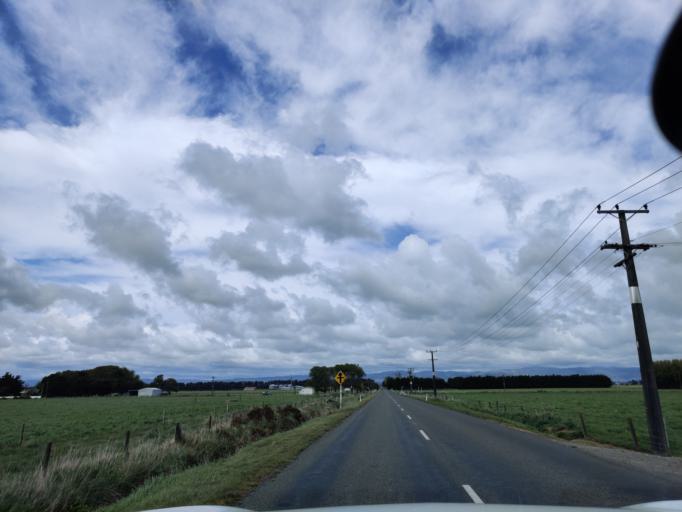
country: NZ
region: Manawatu-Wanganui
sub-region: Palmerston North City
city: Palmerston North
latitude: -40.3329
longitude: 175.5140
